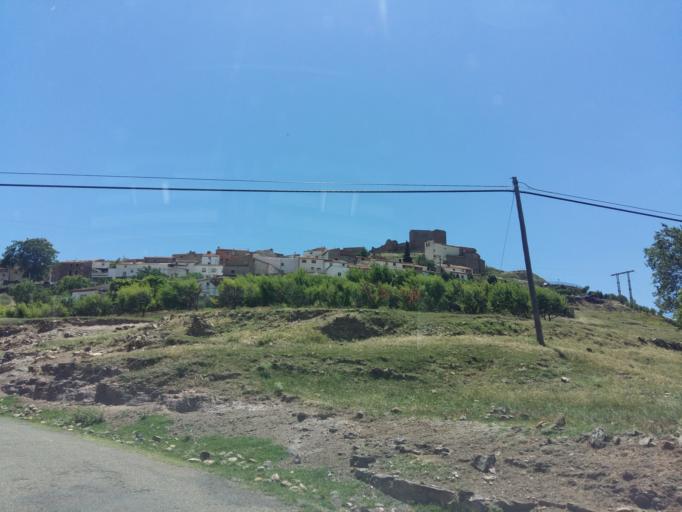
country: ES
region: Aragon
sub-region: Provincia de Zaragoza
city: Trasmoz
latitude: 41.8282
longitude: -1.7224
